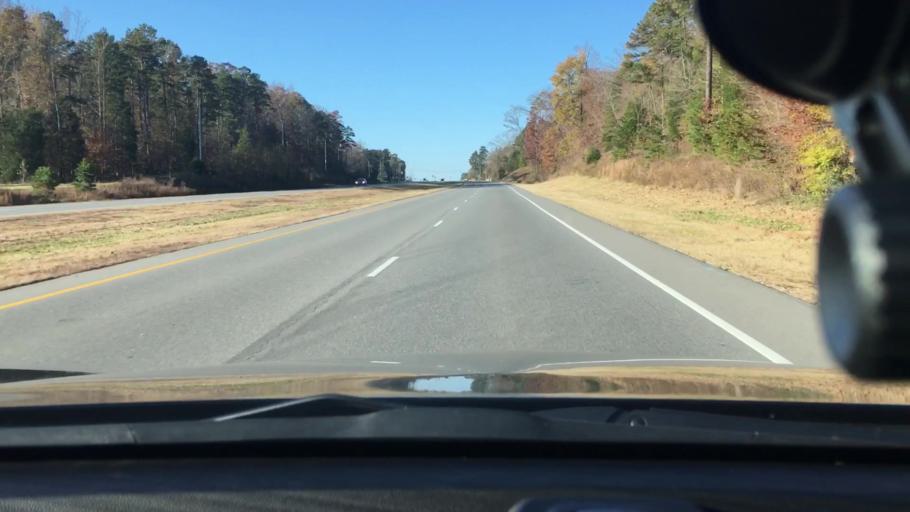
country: US
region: North Carolina
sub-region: Cabarrus County
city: Mount Pleasant
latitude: 35.3973
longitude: -80.4756
